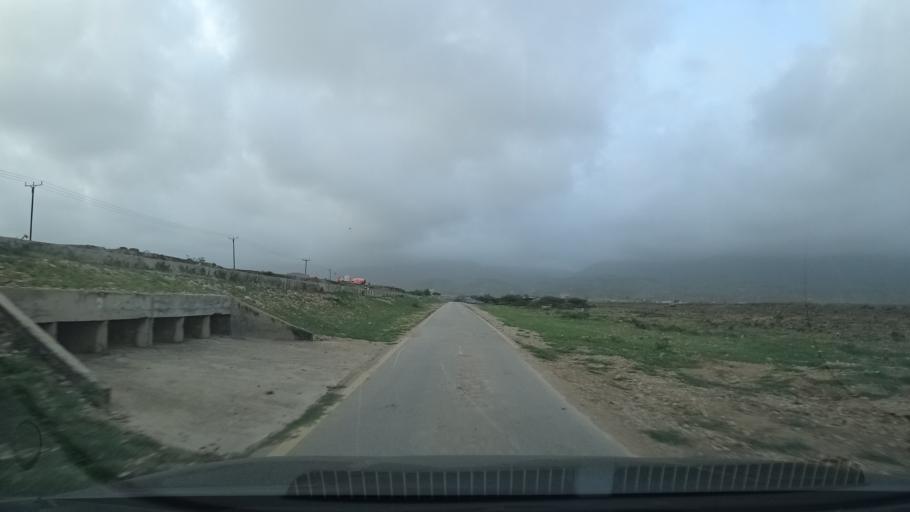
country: OM
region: Zufar
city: Salalah
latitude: 17.0904
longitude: 54.2329
